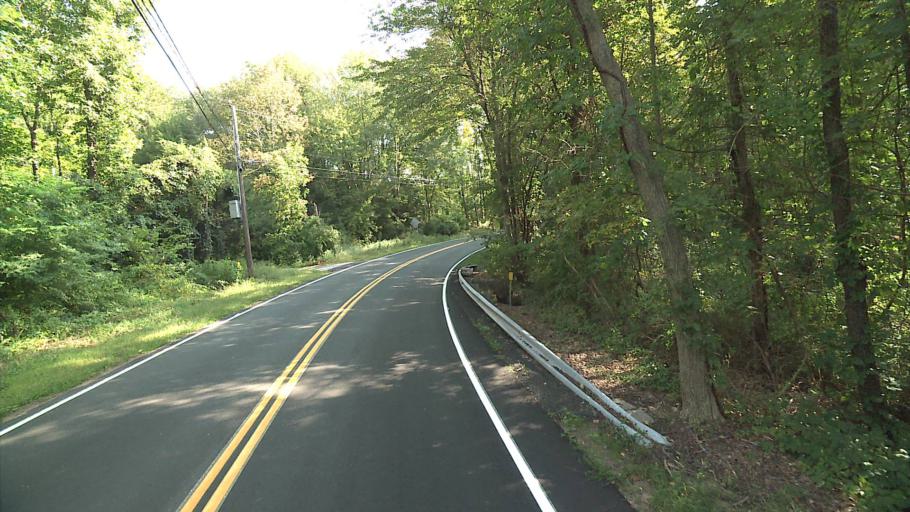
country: US
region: Connecticut
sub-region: Tolland County
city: Coventry Lake
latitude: 41.7305
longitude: -72.3886
